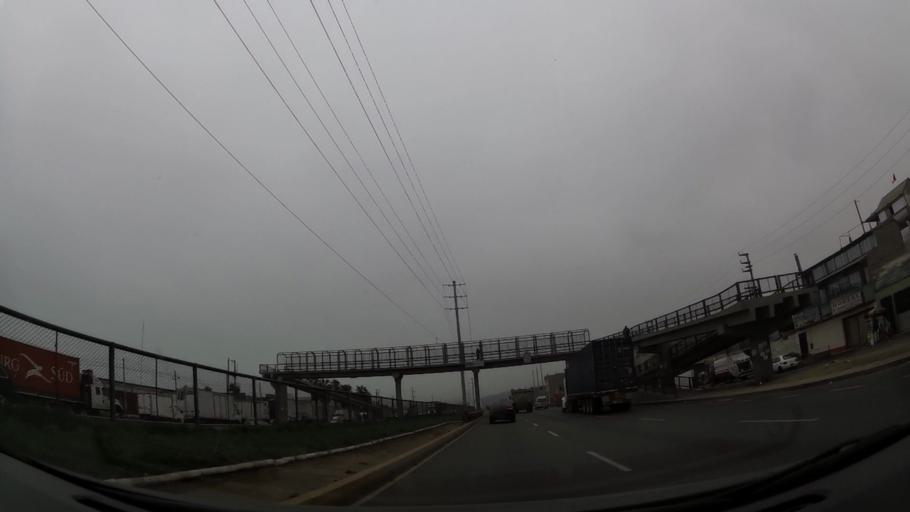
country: PE
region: Lima
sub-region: Lima
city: Independencia
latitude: -11.9728
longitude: -77.1250
